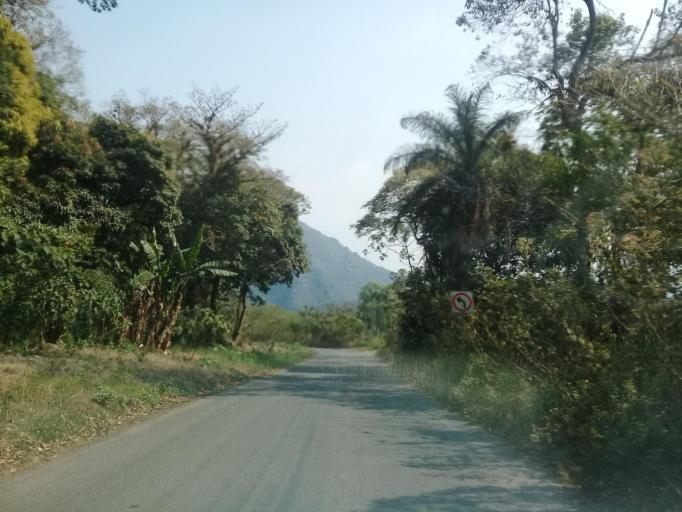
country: MX
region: Veracruz
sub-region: Ixtaczoquitlan
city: Campo Chico
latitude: 18.8316
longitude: -97.0135
